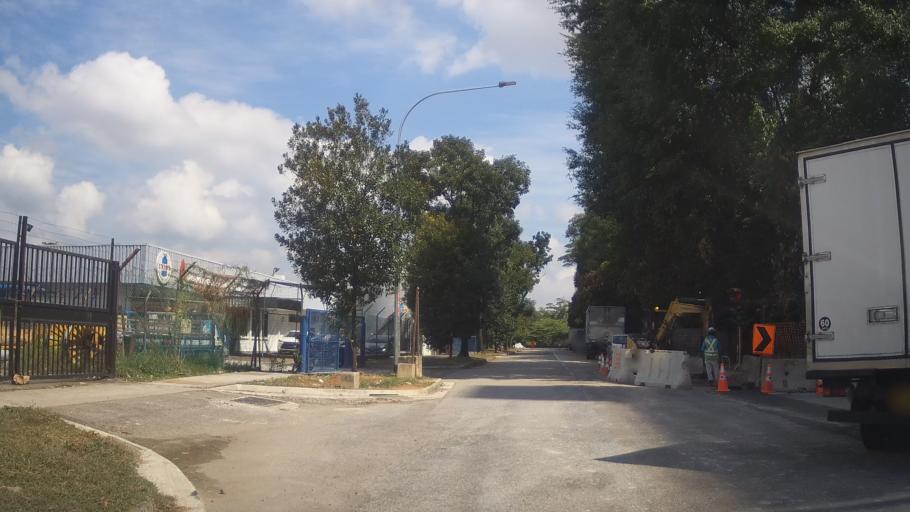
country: SG
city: Singapore
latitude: 1.3174
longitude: 103.7151
